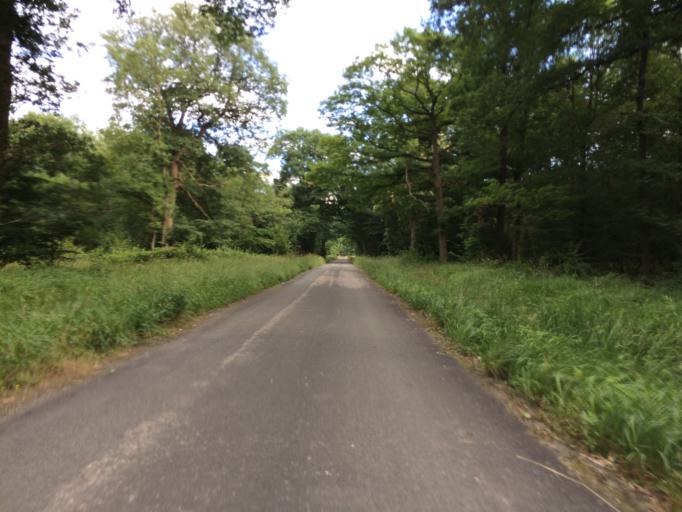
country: FR
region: Ile-de-France
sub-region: Departement de l'Essonne
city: Etiolles
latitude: 48.6598
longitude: 2.4851
